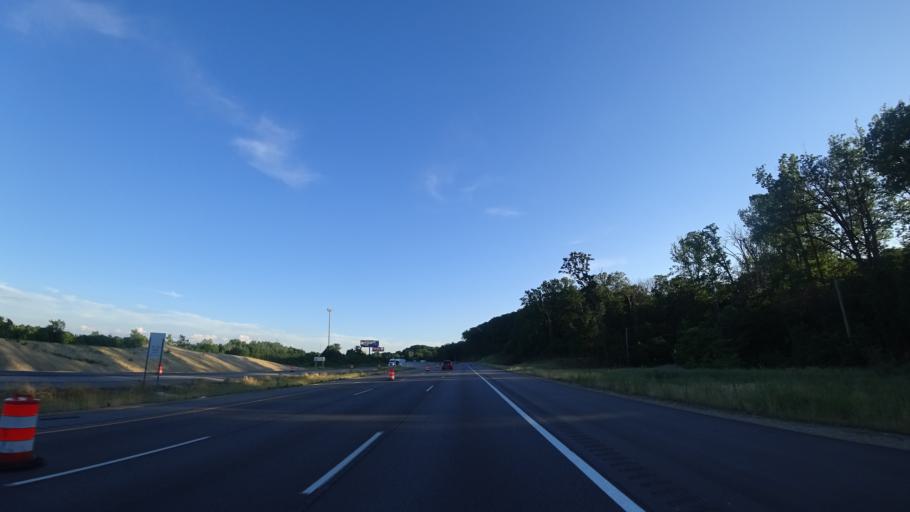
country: US
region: Michigan
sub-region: Berrien County
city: Bridgman
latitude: 41.9387
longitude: -86.5702
